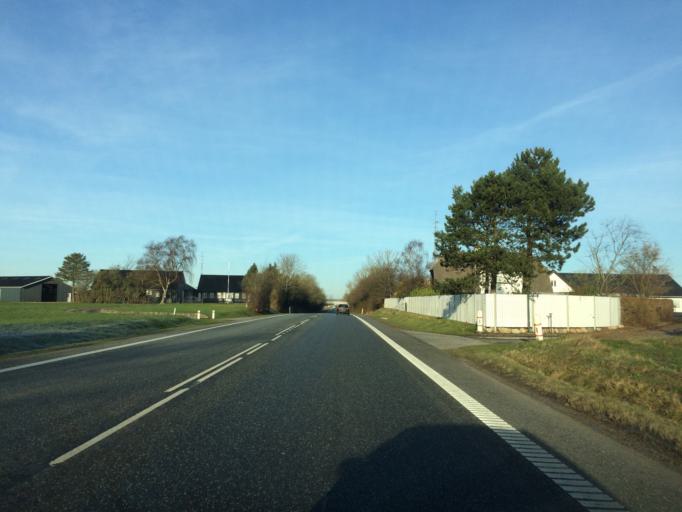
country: DK
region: South Denmark
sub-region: Fredericia Kommune
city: Snoghoj
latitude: 55.5505
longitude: 9.6783
